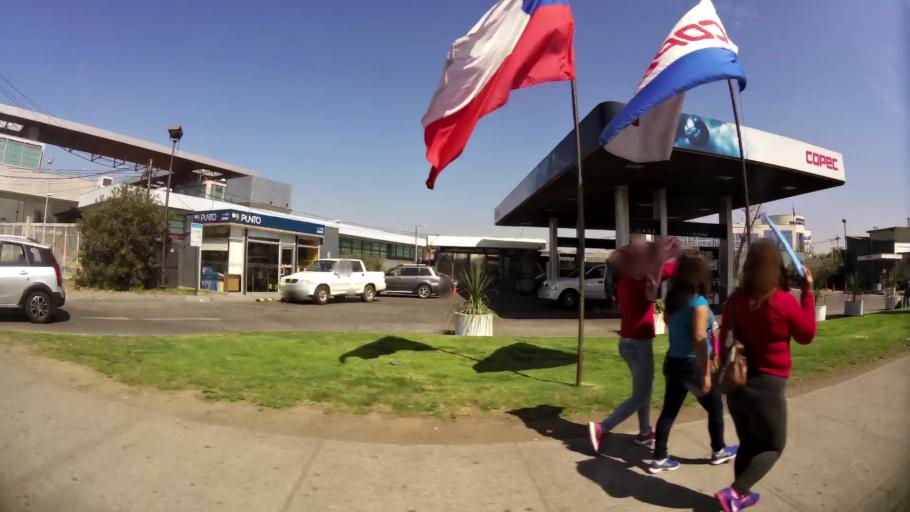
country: CL
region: Santiago Metropolitan
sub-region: Provincia de Santiago
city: Santiago
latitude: -33.4721
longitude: -70.6562
